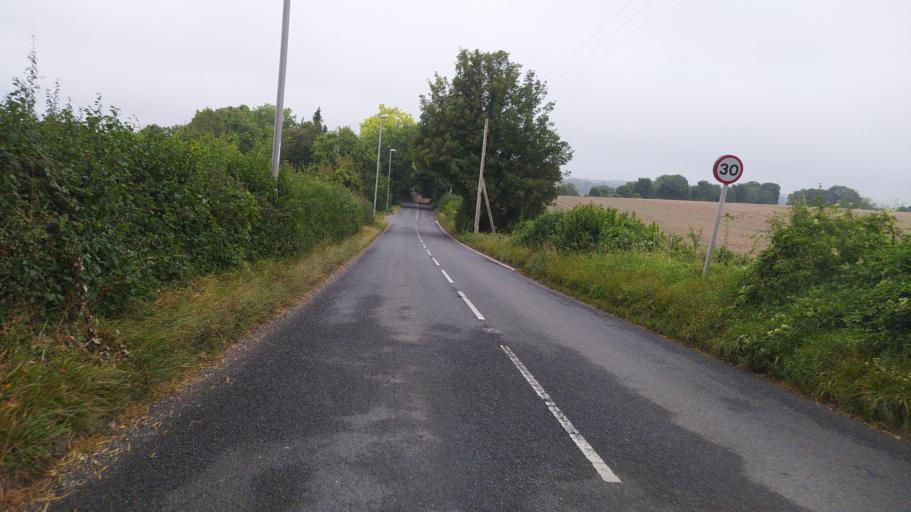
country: GB
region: England
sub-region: Wiltshire
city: Bower Chalke
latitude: 50.9506
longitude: -1.9996
